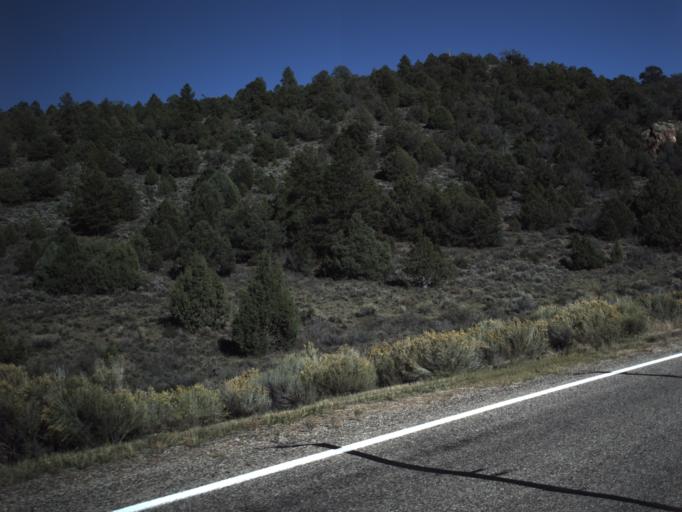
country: US
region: Utah
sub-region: Garfield County
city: Panguitch
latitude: 37.7669
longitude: -112.5336
